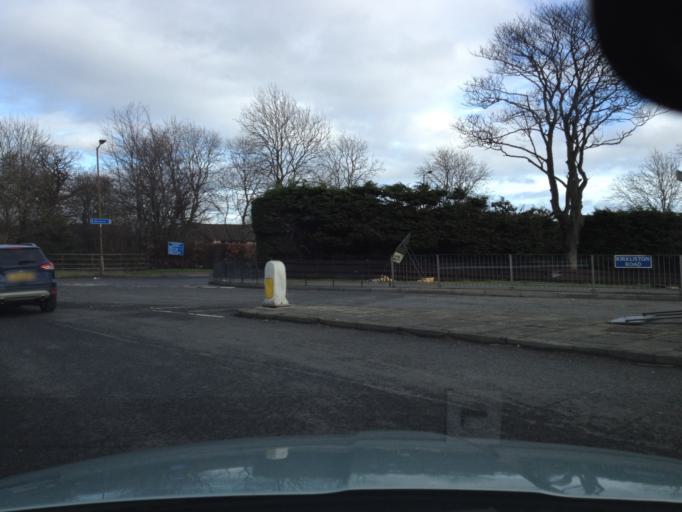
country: GB
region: Scotland
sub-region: Edinburgh
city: Queensferry
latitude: 55.9834
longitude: -3.3970
